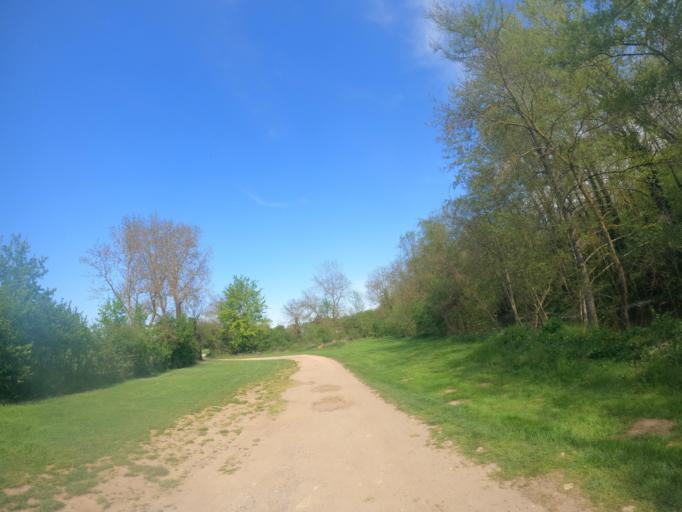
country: FR
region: Poitou-Charentes
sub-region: Departement des Deux-Sevres
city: Saint-Varent
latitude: 46.9141
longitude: -0.2054
